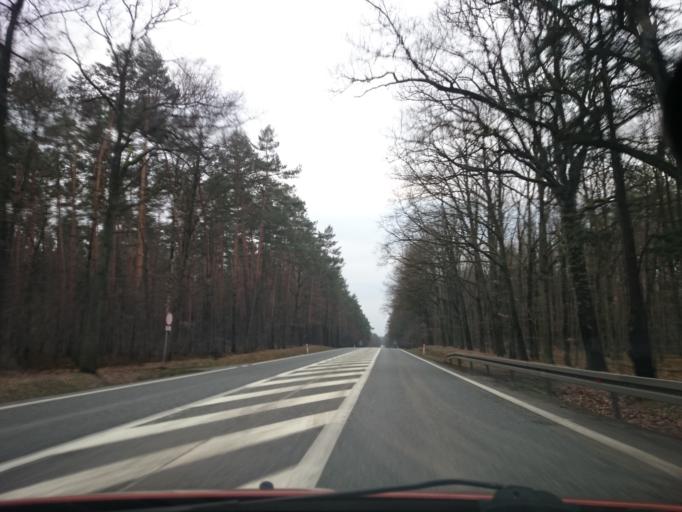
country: PL
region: Opole Voivodeship
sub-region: Powiat opolski
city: Dabrowa
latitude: 50.6855
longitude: 17.7272
